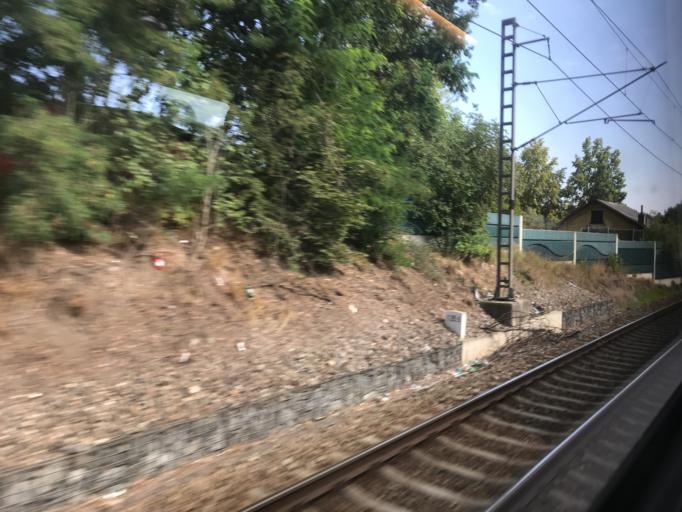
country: CZ
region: Central Bohemia
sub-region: Okres Benesov
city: Benesov
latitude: 49.7870
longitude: 14.6851
